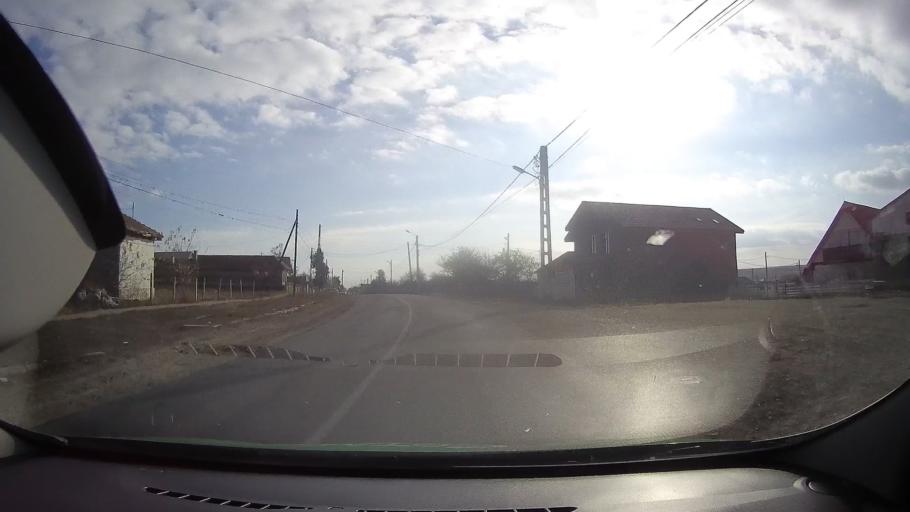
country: RO
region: Constanta
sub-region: Comuna Corbu
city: Corbu
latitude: 44.4060
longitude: 28.6616
